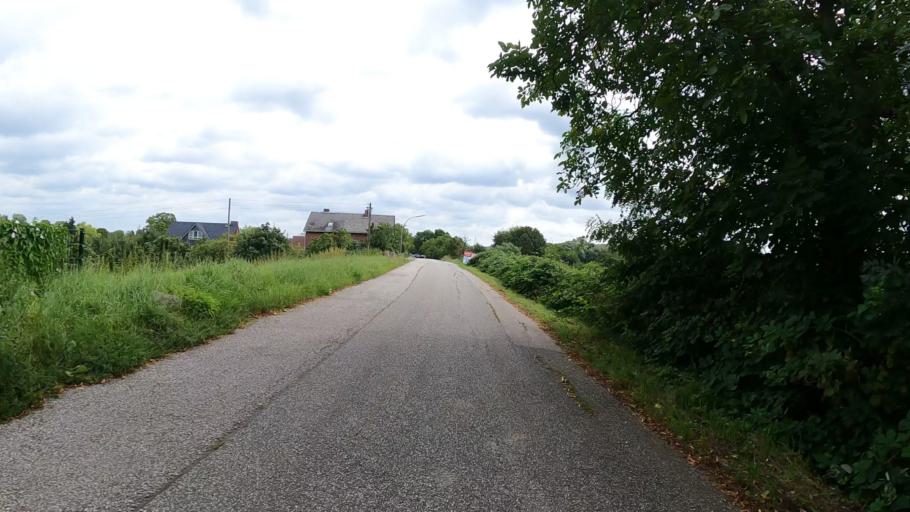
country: DE
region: Lower Saxony
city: Neu Wulmstorf
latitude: 53.5192
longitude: 9.8511
